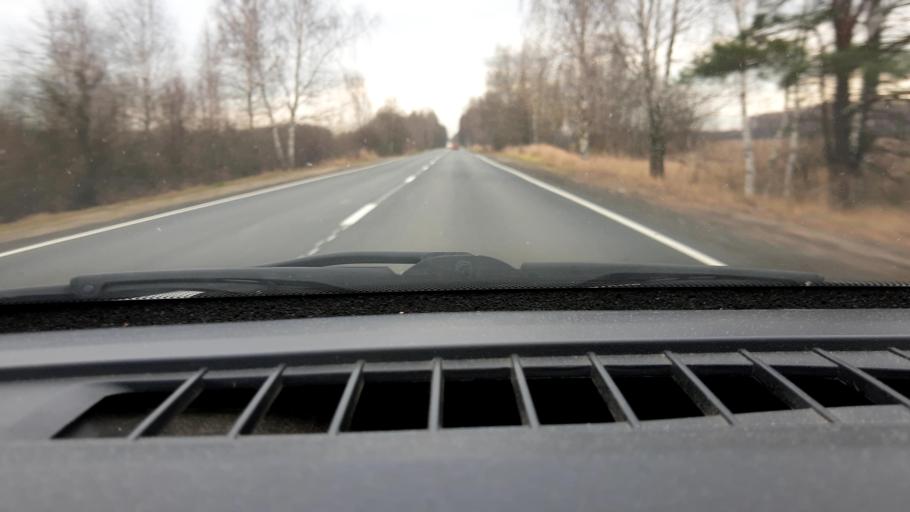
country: RU
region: Nizjnij Novgorod
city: Novaya Balakhna
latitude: 56.5591
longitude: 43.7317
